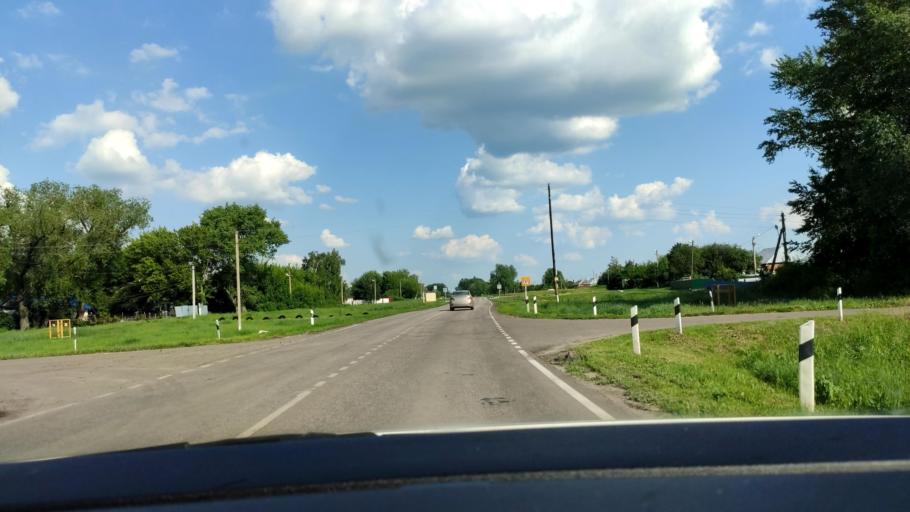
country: RU
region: Voronezj
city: Verkhnyaya Khava
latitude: 51.6724
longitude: 39.9521
